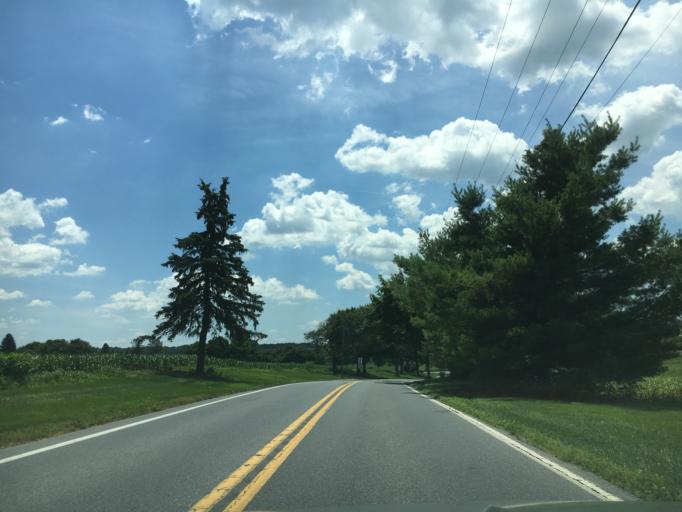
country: US
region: Pennsylvania
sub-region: Lehigh County
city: Schnecksville
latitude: 40.6376
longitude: -75.5770
